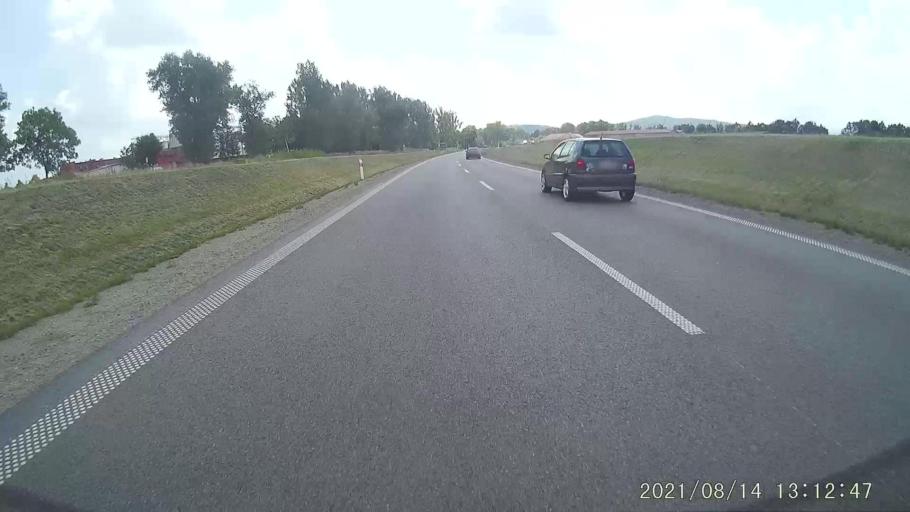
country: PL
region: Lower Silesian Voivodeship
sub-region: Powiat klodzki
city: Klodzko
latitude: 50.3937
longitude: 16.6585
